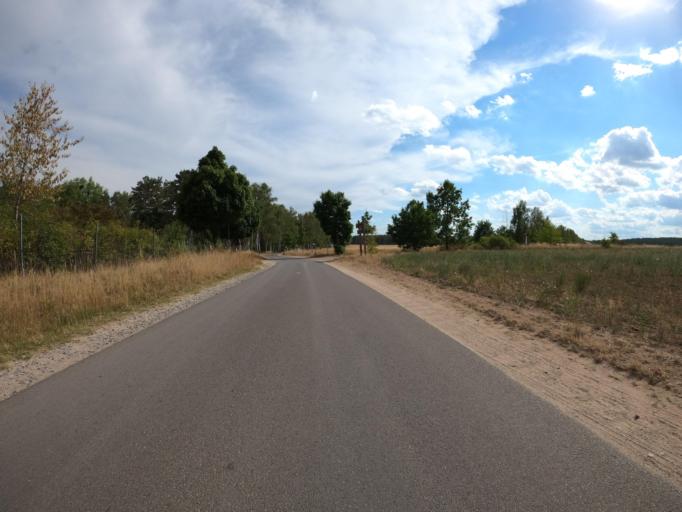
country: DE
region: Brandenburg
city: Lychen
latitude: 53.2965
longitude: 13.4283
